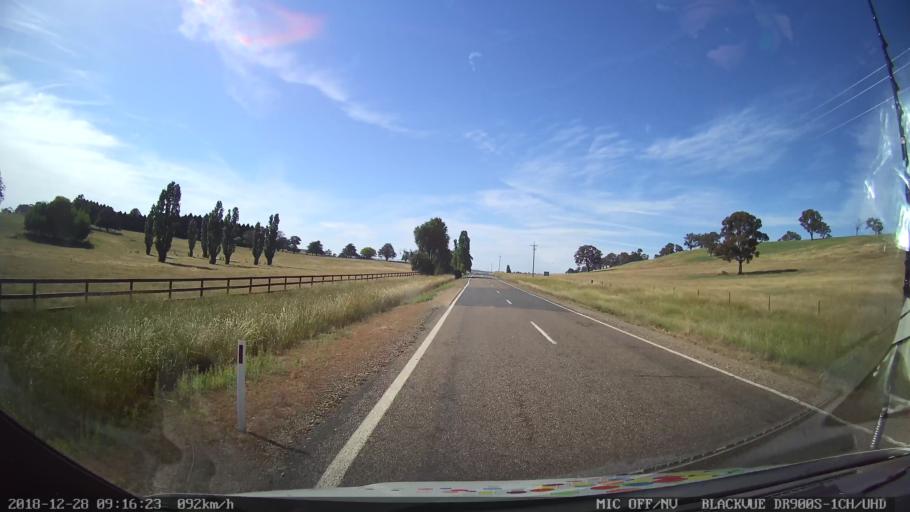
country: AU
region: New South Wales
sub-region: Upper Lachlan Shire
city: Crookwell
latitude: -34.3077
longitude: 149.3553
